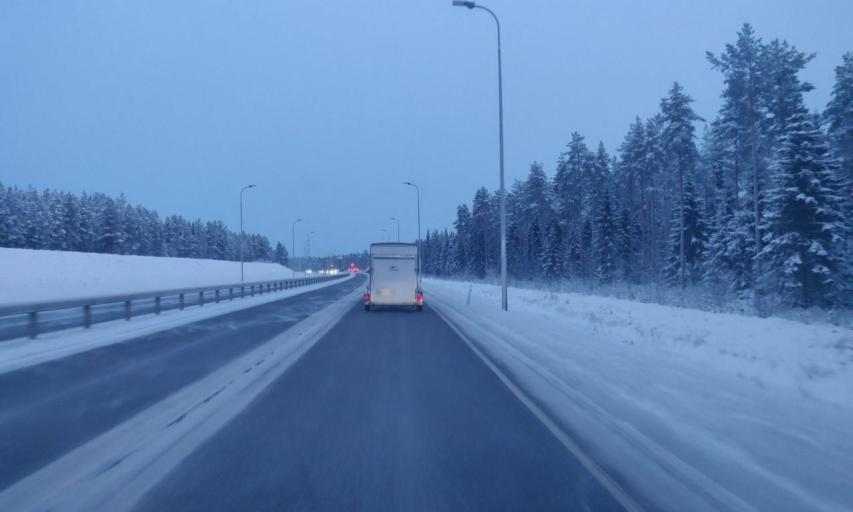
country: FI
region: Northern Ostrobothnia
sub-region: Oulu
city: Kempele
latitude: 64.9828
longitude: 25.5538
